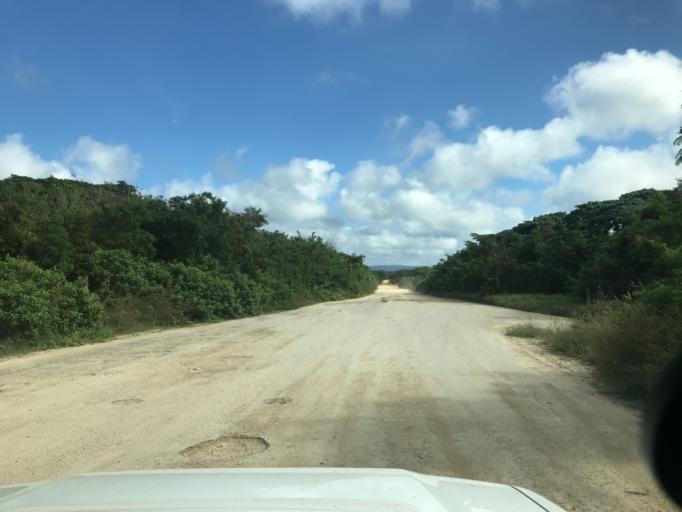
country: VU
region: Sanma
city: Luganville
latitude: -15.5199
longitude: 167.1371
